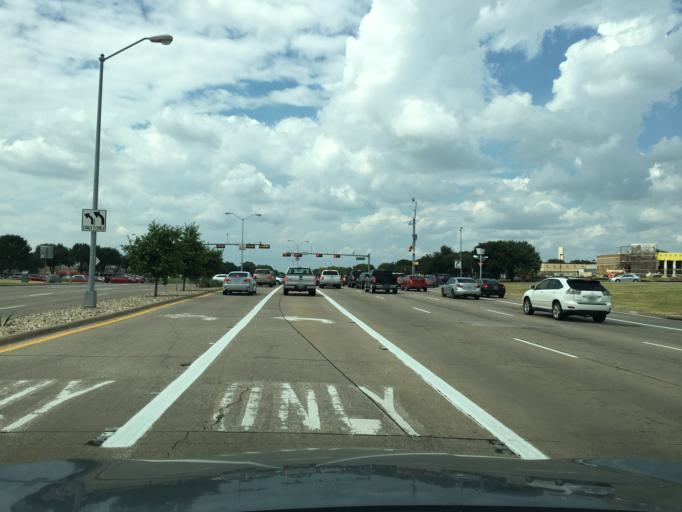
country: US
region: Texas
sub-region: Dallas County
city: Addison
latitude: 33.0263
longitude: -96.7950
